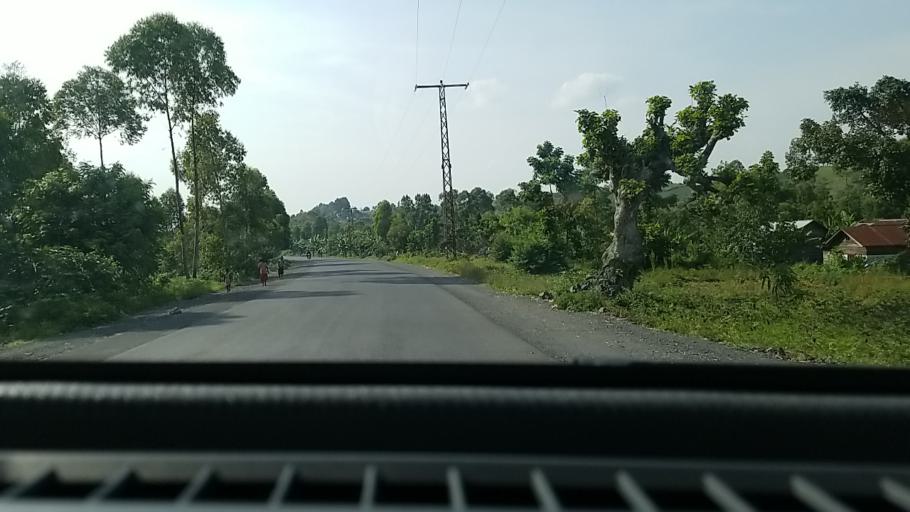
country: CD
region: Nord Kivu
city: Sake
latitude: -1.6092
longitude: 29.1382
